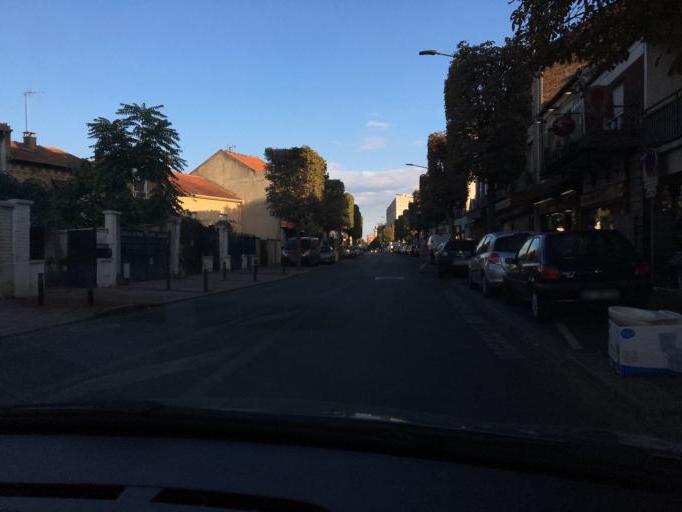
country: FR
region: Ile-de-France
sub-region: Departement du Val-de-Marne
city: Fontenay-sous-Bois
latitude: 48.8536
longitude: 2.4699
